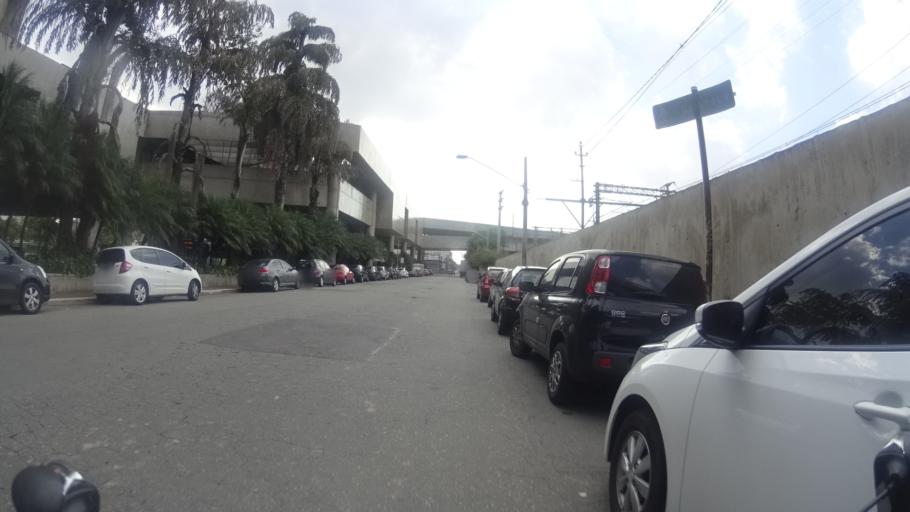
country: BR
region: Sao Paulo
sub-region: Sao Paulo
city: Sao Paulo
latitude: -23.5477
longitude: -46.6151
